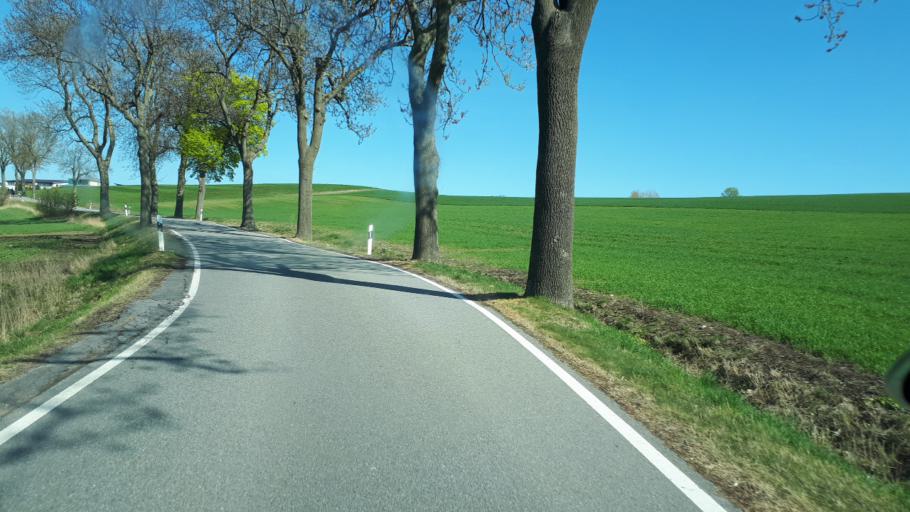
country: DE
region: Saxony
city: Burkhardtsdorf
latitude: 50.7615
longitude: 12.9299
